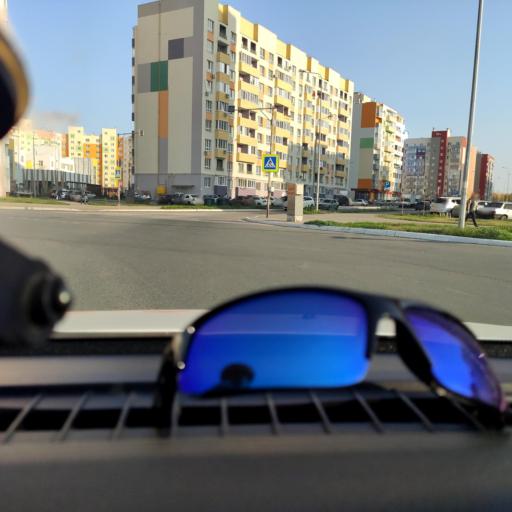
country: RU
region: Samara
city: Samara
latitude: 53.0952
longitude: 50.1597
